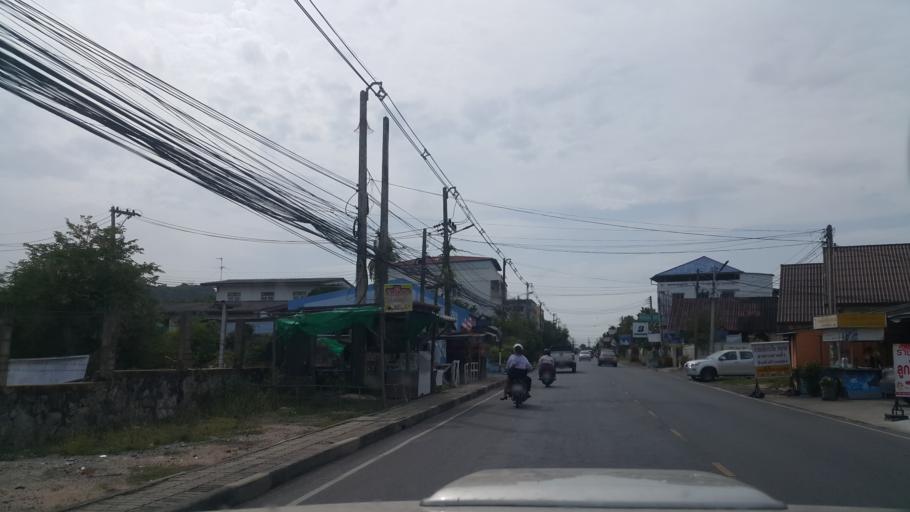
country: TH
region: Rayong
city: Ban Chang
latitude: 12.7298
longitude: 101.0509
